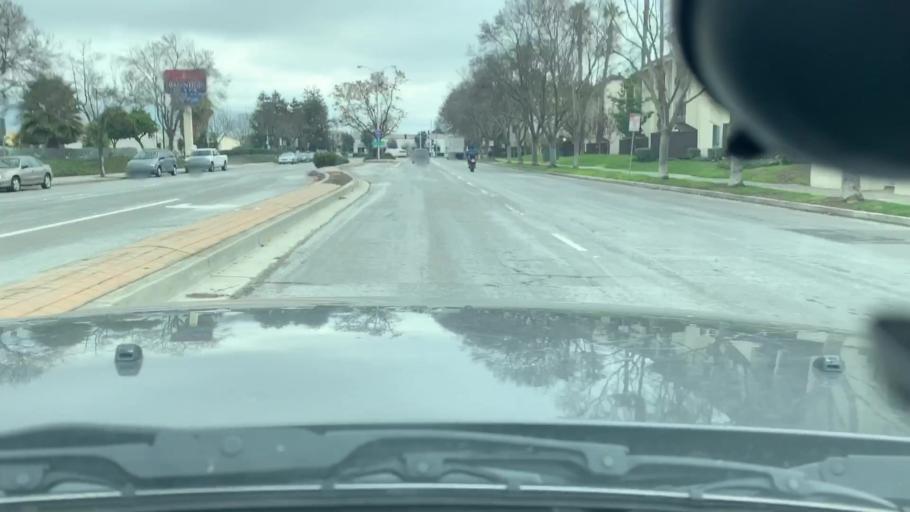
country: US
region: California
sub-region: Alameda County
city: Fremont
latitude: 37.5191
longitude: -121.9934
